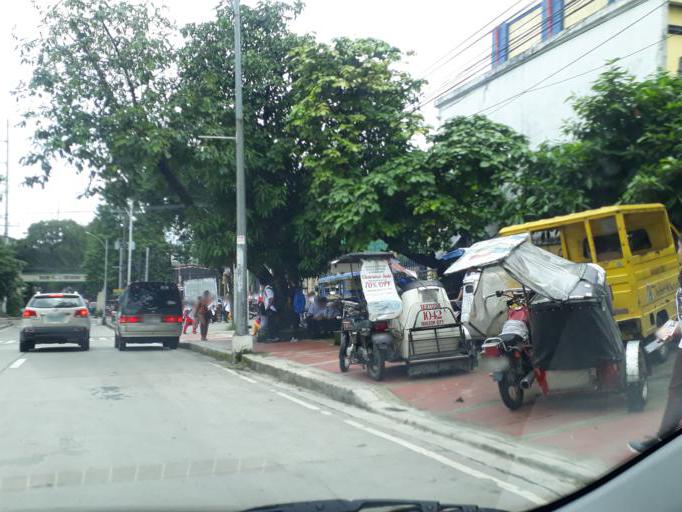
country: PH
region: Calabarzon
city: Del Monte
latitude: 14.6294
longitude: 121.0252
